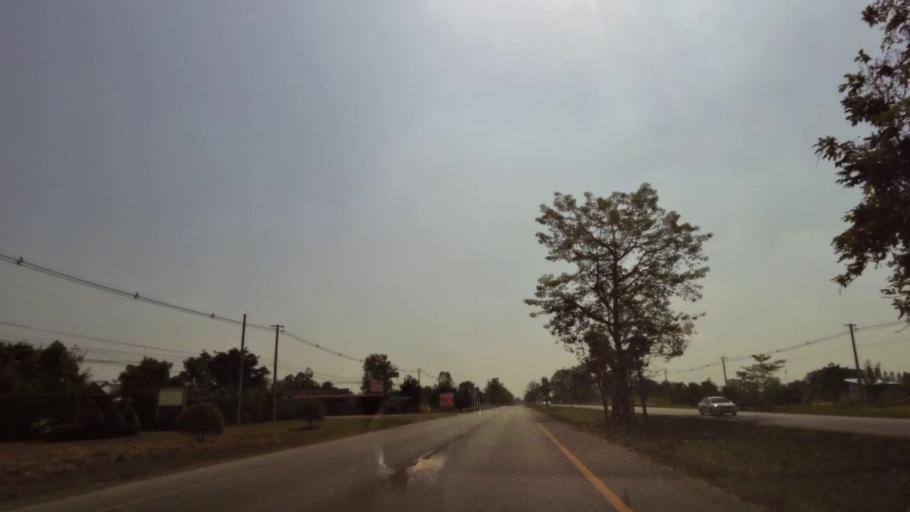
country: TH
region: Phichit
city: Bueng Na Rang
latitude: 16.3045
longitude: 100.1285
